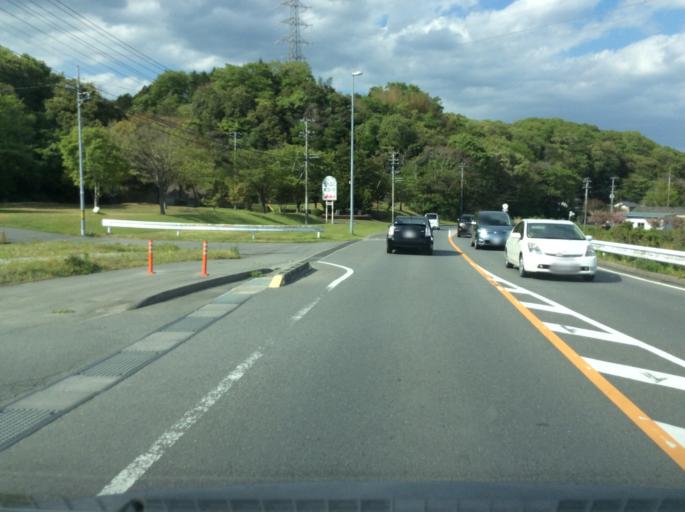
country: JP
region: Fukushima
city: Iwaki
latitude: 36.9336
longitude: 140.8292
